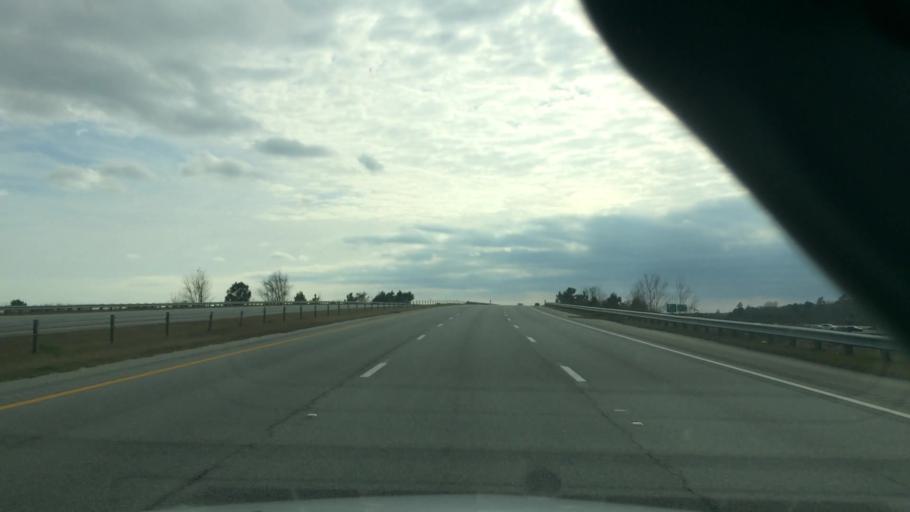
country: US
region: South Carolina
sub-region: Horry County
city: North Myrtle Beach
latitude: 33.8472
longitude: -78.7000
